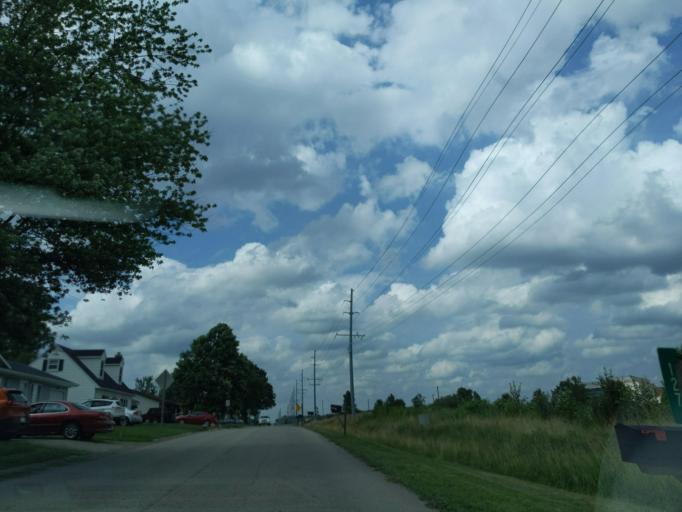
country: US
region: Indiana
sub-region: Ripley County
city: Batesville
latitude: 39.3109
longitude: -85.2083
